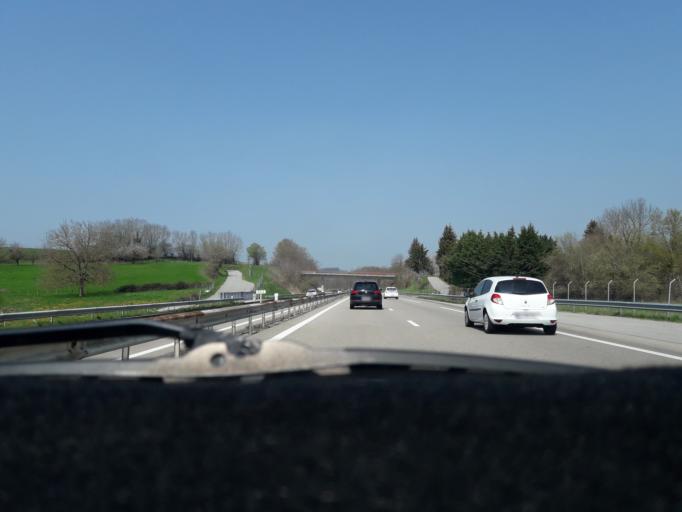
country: FR
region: Rhone-Alpes
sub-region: Departement de l'Isere
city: Chabons
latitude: 45.4327
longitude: 5.4232
